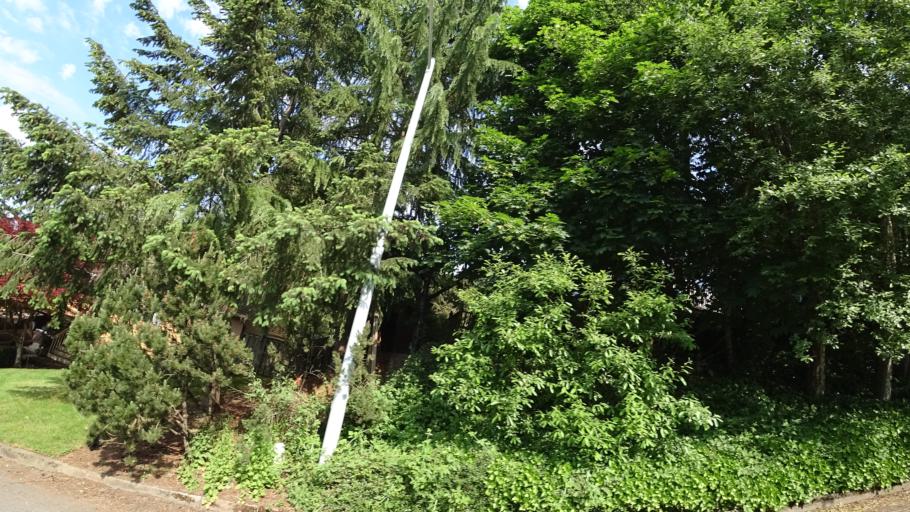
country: US
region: Oregon
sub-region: Washington County
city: Garden Home-Whitford
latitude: 45.4569
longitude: -122.7441
